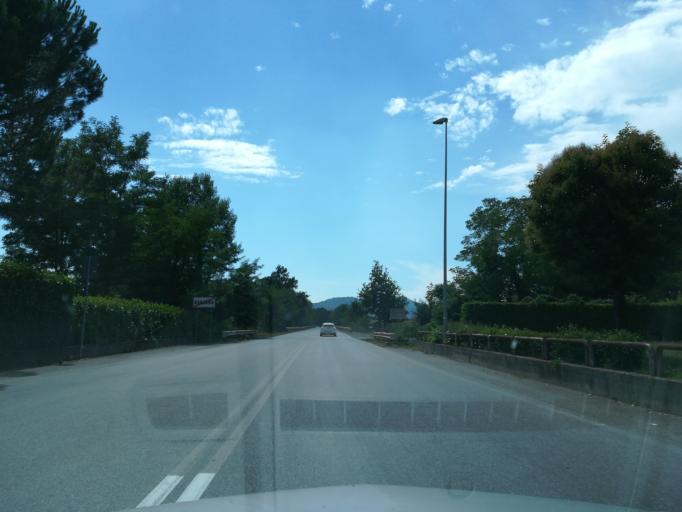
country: IT
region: Lombardy
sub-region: Provincia di Bergamo
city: Barzana
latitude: 45.7297
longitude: 9.5717
